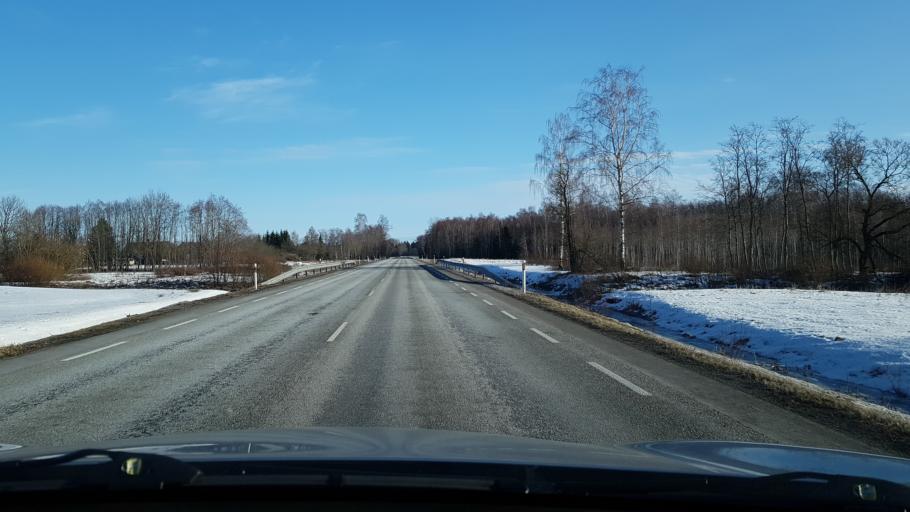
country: EE
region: Viljandimaa
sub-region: Vohma linn
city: Vohma
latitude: 58.6620
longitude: 25.6194
